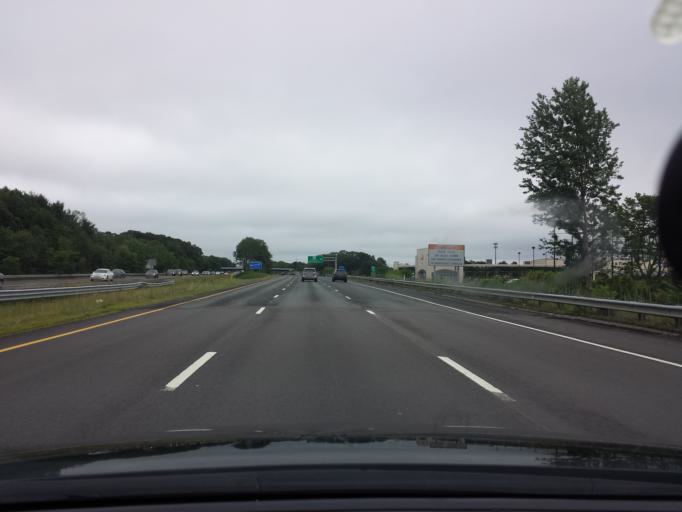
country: US
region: Massachusetts
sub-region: Bristol County
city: Seekonk
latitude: 41.8053
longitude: -71.3371
